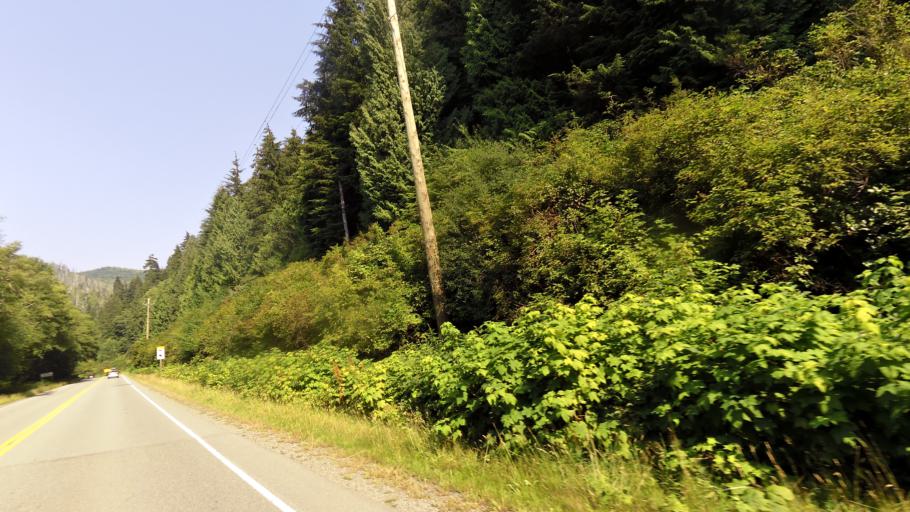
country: CA
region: British Columbia
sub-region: Regional District of Alberni-Clayoquot
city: Ucluelet
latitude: 49.0634
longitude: -125.4717
